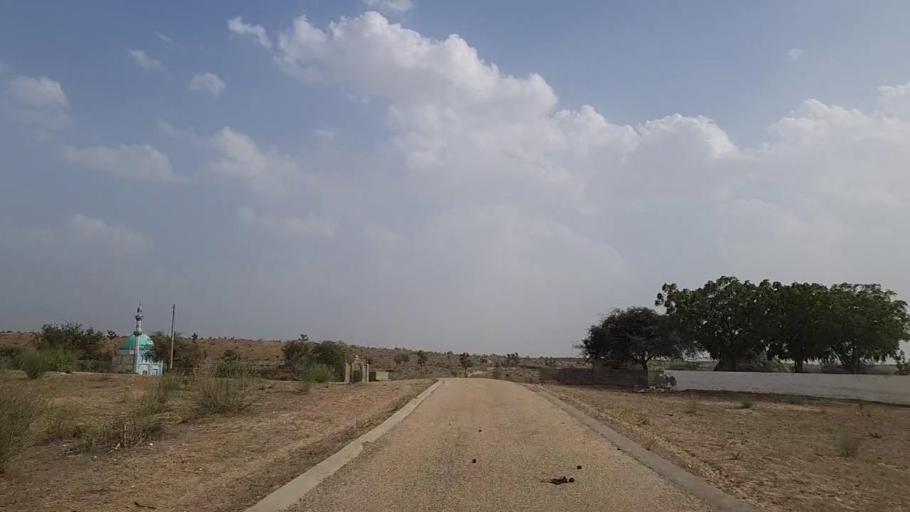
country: PK
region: Sindh
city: Islamkot
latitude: 24.8615
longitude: 70.1128
